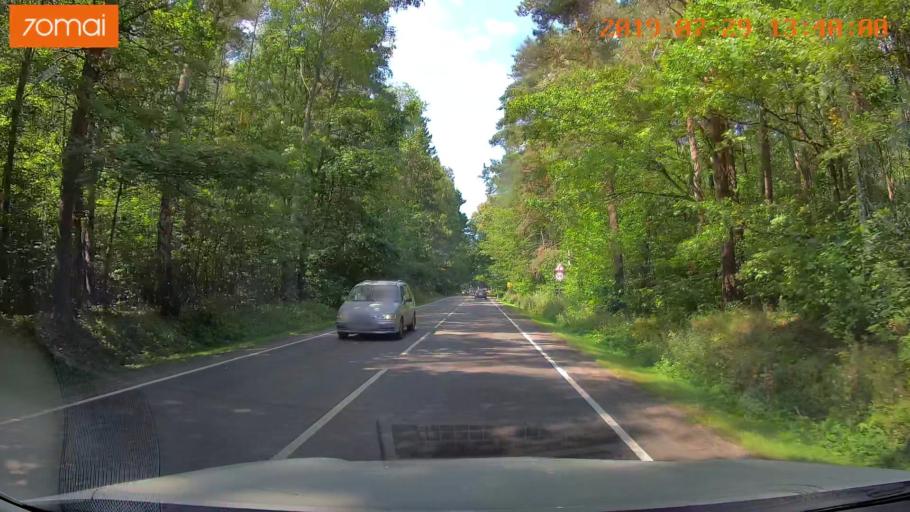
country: RU
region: Kaliningrad
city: Svetlyy
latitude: 54.7258
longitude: 20.1438
